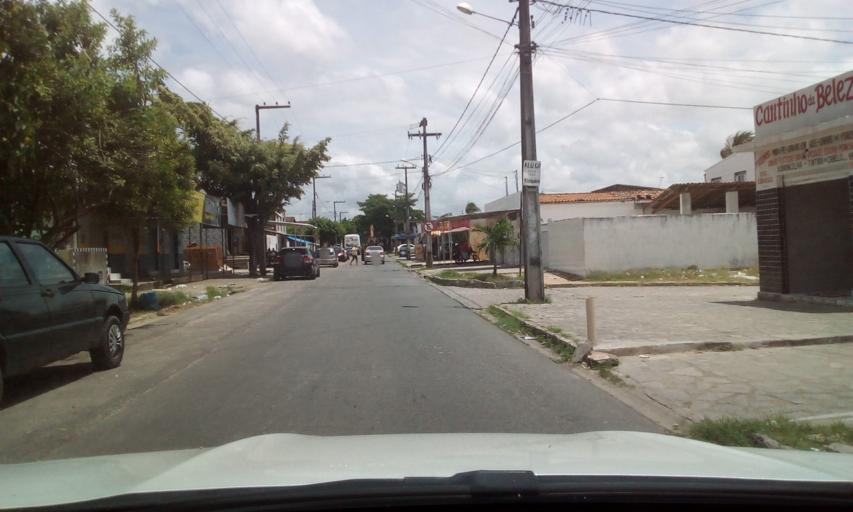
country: BR
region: Paraiba
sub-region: Joao Pessoa
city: Joao Pessoa
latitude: -7.1810
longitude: -34.8826
